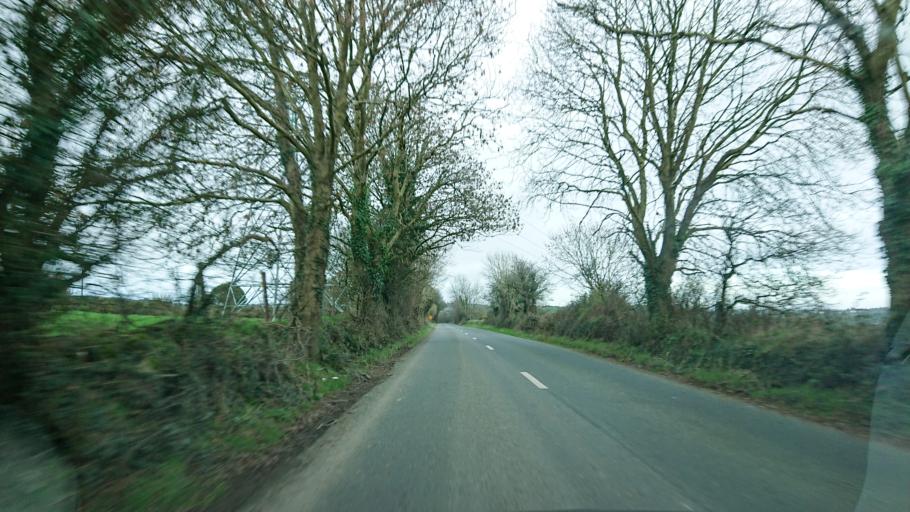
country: IE
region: Leinster
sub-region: Kilkenny
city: Mooncoin
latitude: 52.2097
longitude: -7.2463
